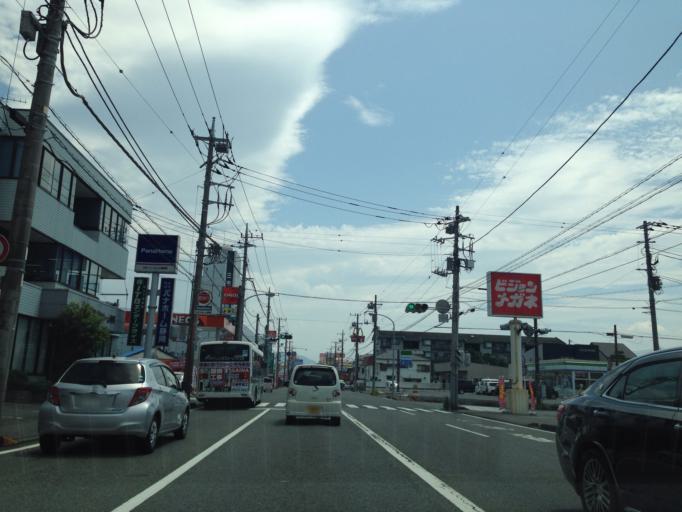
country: JP
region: Shizuoka
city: Numazu
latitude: 35.0883
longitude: 138.8671
